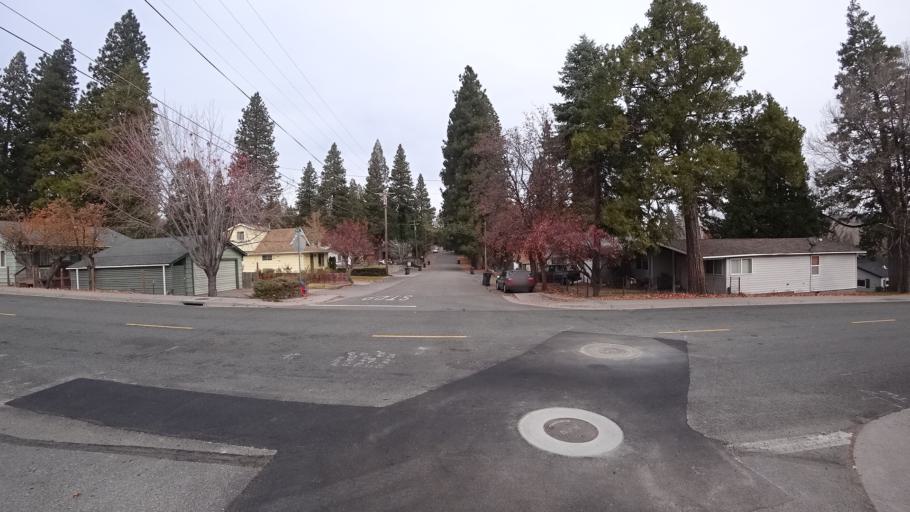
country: US
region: California
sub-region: Siskiyou County
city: Weed
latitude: 41.4164
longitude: -122.3858
